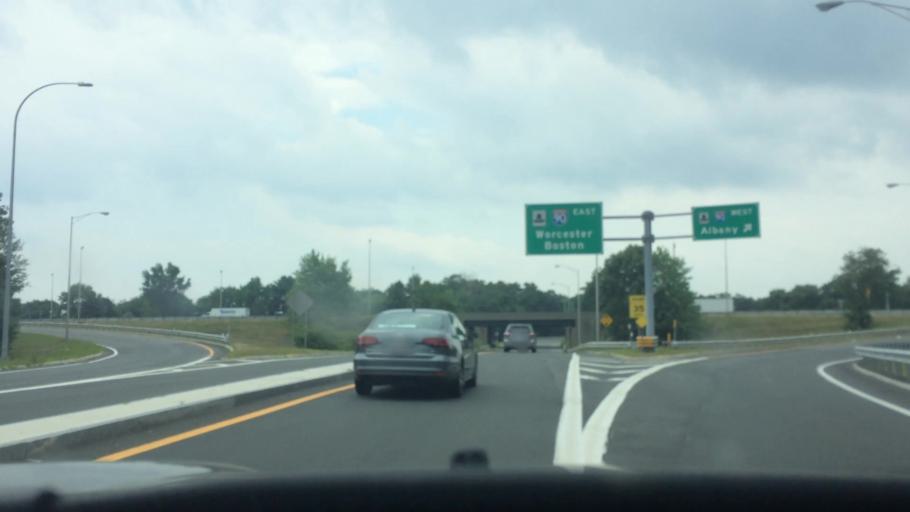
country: US
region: Massachusetts
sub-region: Hampden County
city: North Chicopee
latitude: 42.1712
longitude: -72.5809
